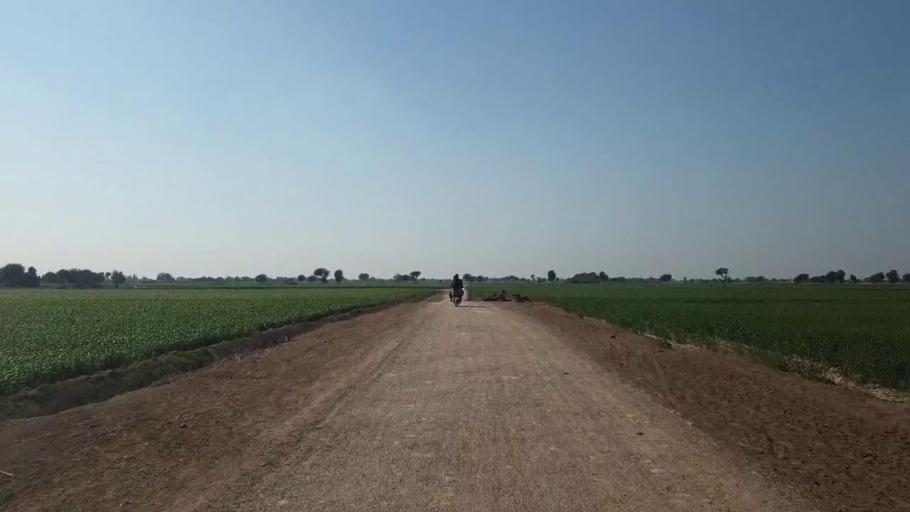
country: PK
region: Sindh
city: Shahdadpur
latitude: 25.9655
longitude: 68.6384
